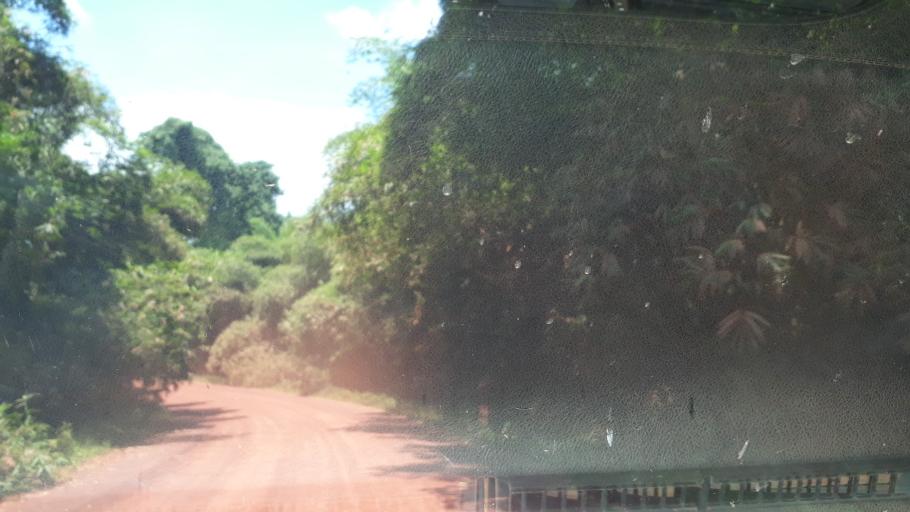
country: CD
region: Eastern Province
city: Kisangani
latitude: 0.5723
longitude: 25.9481
